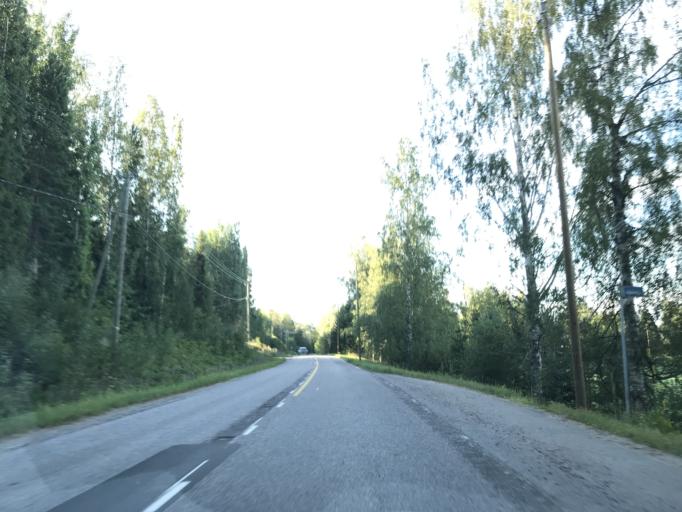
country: FI
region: Uusimaa
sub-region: Helsinki
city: Nurmijaervi
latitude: 60.3716
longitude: 24.6788
